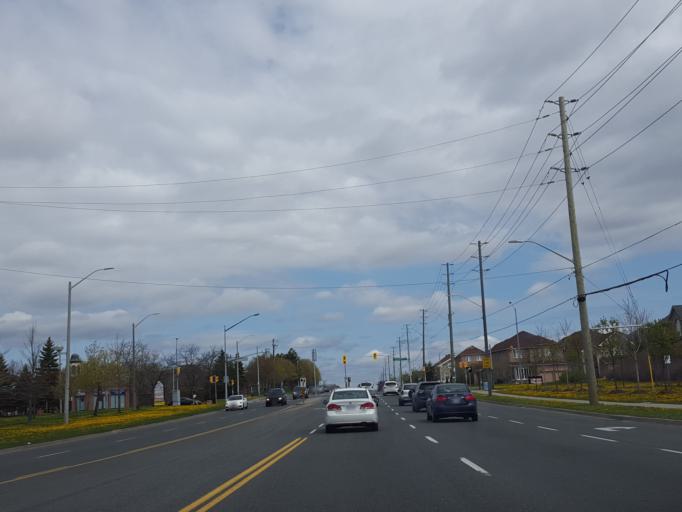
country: CA
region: Ontario
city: Markham
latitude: 43.8394
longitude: -79.2516
